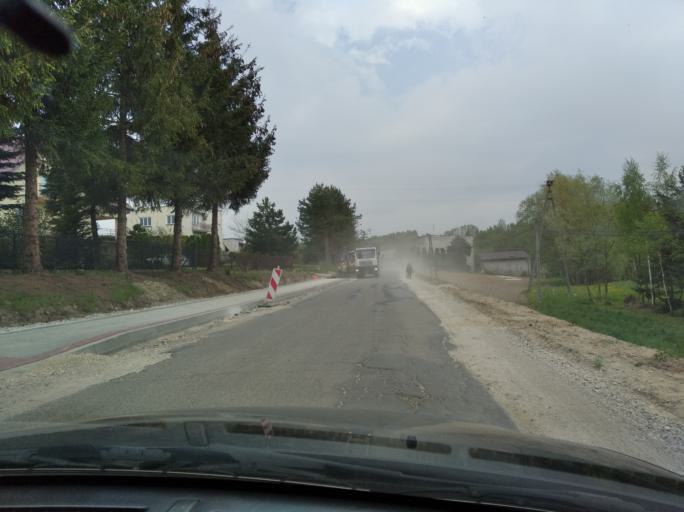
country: PL
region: Lesser Poland Voivodeship
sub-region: Powiat tarnowski
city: Skrzyszow
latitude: 49.9787
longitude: 21.0649
